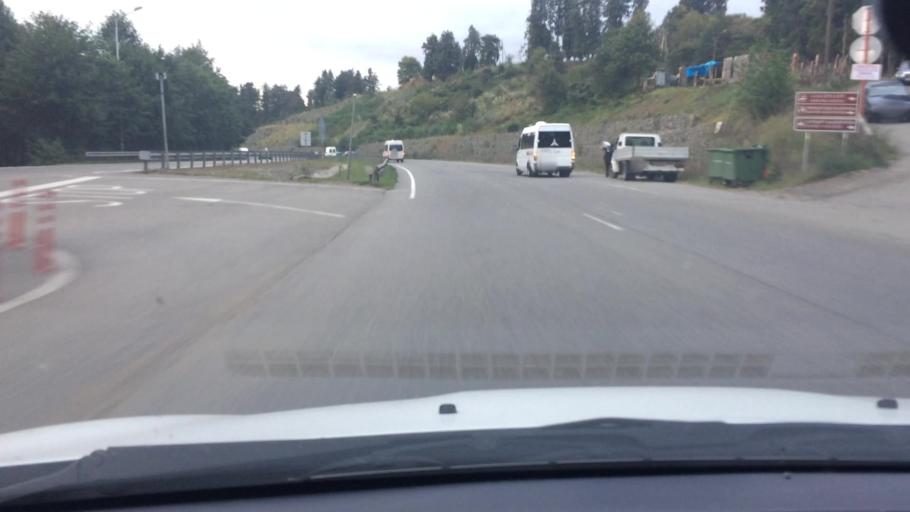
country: GE
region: Ajaria
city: Makhinjauri
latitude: 41.6940
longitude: 41.7252
